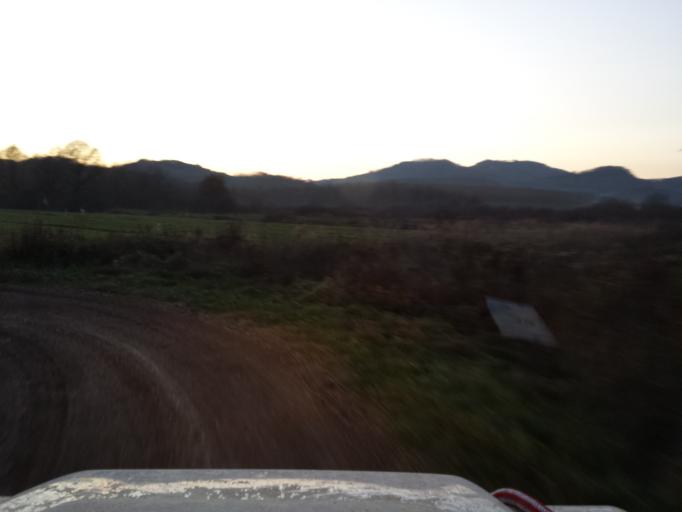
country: IT
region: Friuli Venezia Giulia
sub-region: Provincia di Gorizia
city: Capriva del Friuli
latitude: 45.9666
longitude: 13.5142
